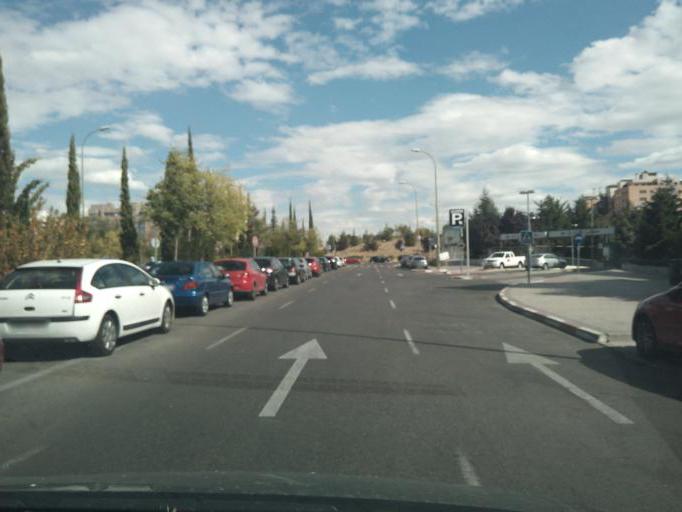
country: ES
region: Madrid
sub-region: Provincia de Madrid
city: Las Tablas
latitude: 40.4981
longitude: -3.6601
